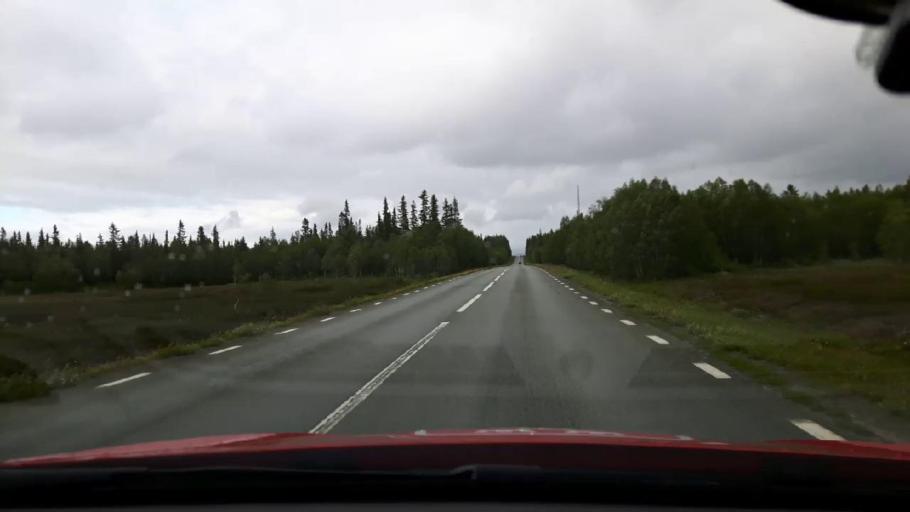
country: SE
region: Jaemtland
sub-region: Are Kommun
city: Are
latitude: 63.3564
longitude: 12.5963
